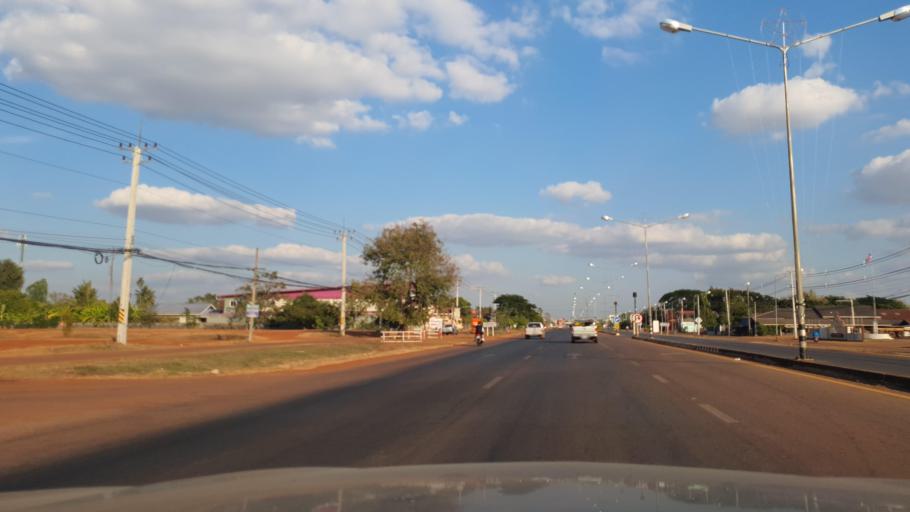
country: TH
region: Sakon Nakhon
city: Sakon Nakhon
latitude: 17.2567
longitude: 104.1731
